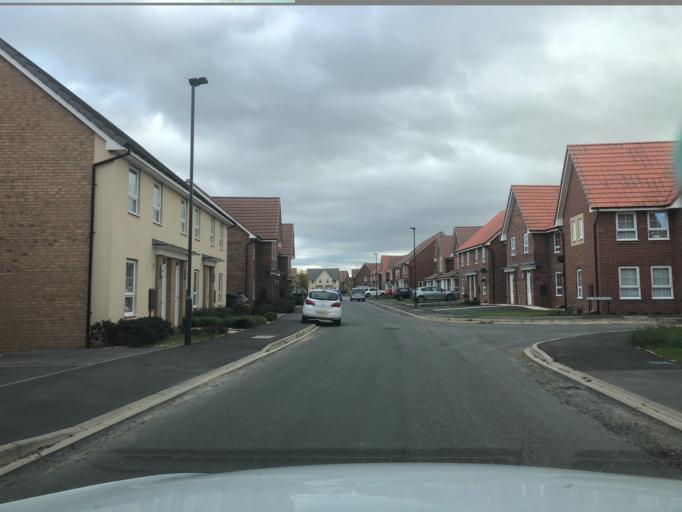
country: GB
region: England
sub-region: North Yorkshire
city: Northallerton
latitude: 54.3447
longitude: -1.4451
